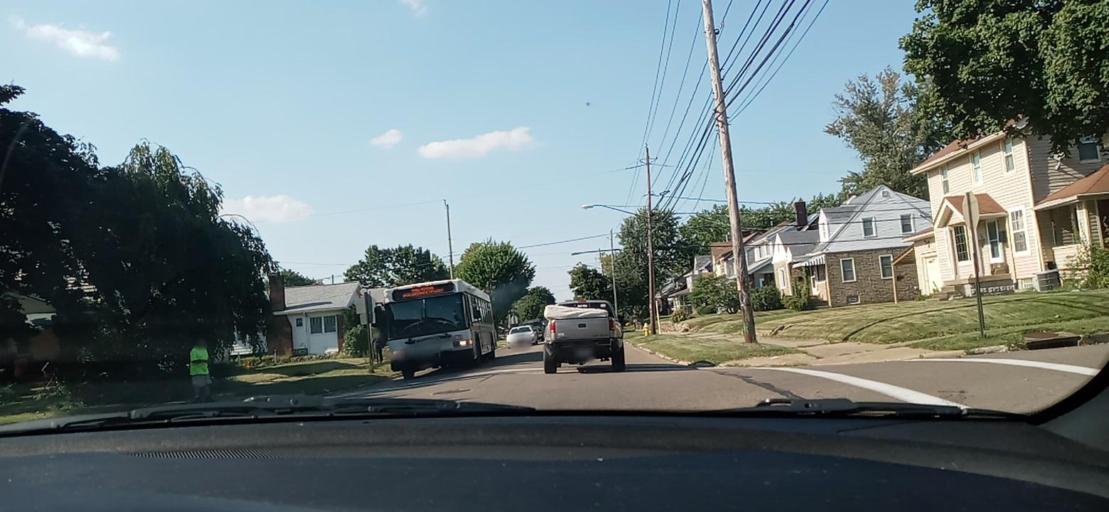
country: US
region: Ohio
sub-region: Summit County
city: Portage Lakes
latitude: 41.0424
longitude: -81.5103
